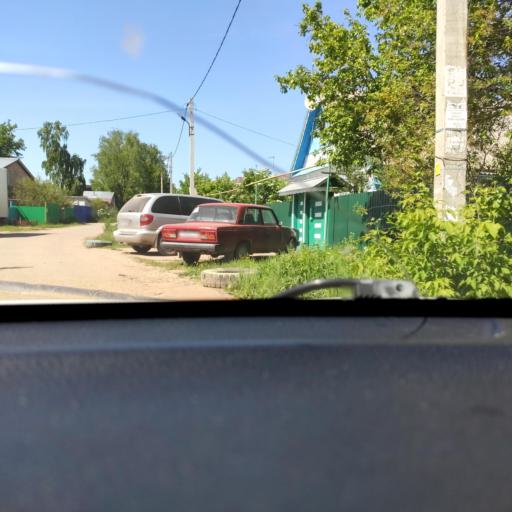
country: RU
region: Tatarstan
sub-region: Gorod Kazan'
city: Kazan
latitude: 55.8595
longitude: 49.1986
